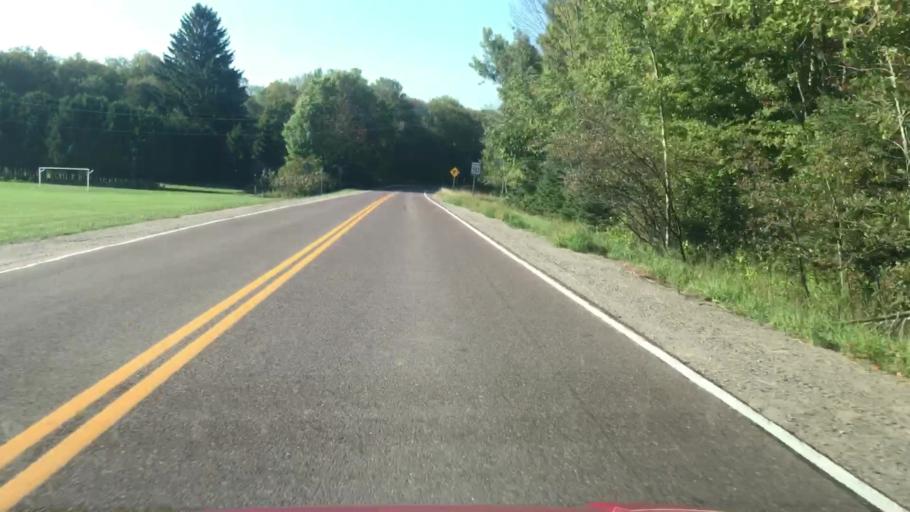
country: US
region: Michigan
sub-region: Chippewa County
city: Sault Ste. Marie
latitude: 46.2795
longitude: -84.0310
